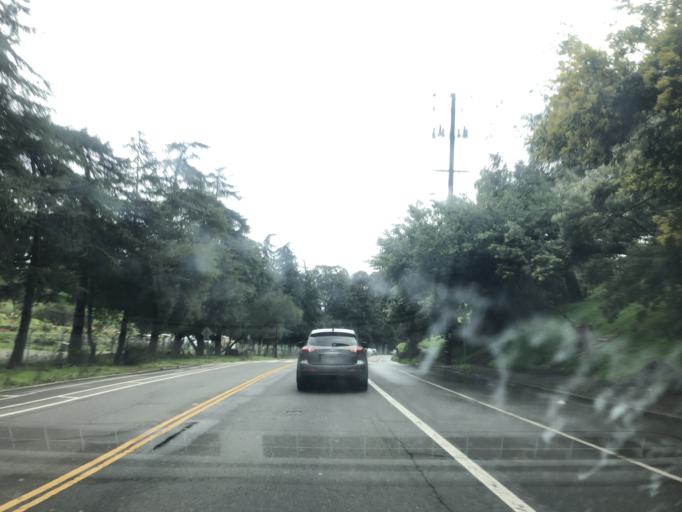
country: US
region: California
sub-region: Alameda County
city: Alameda
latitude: 37.7812
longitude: -122.1874
